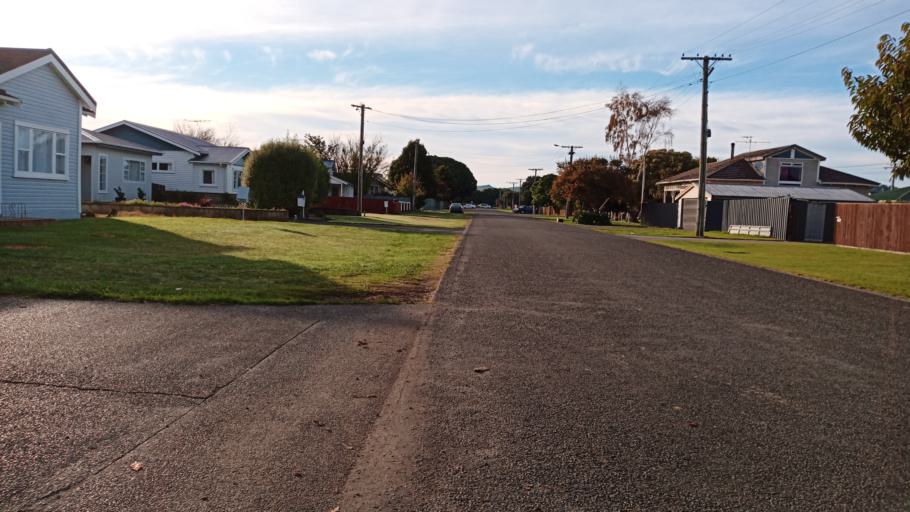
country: NZ
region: Gisborne
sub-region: Gisborne District
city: Gisborne
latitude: -38.6577
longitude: 178.0053
